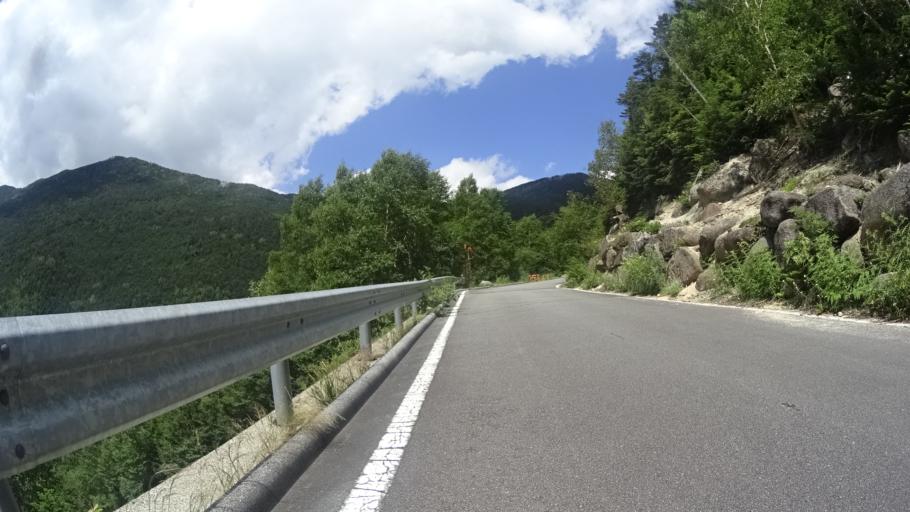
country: JP
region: Yamanashi
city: Enzan
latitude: 35.8669
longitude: 138.6574
